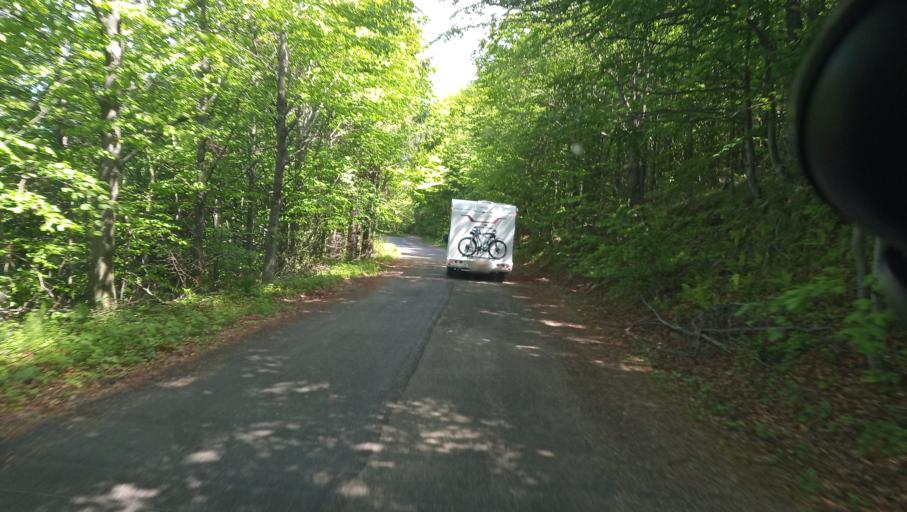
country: RO
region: Caras-Severin
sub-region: Comuna Valiug
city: Valiug
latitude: 45.2044
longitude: 22.0572
